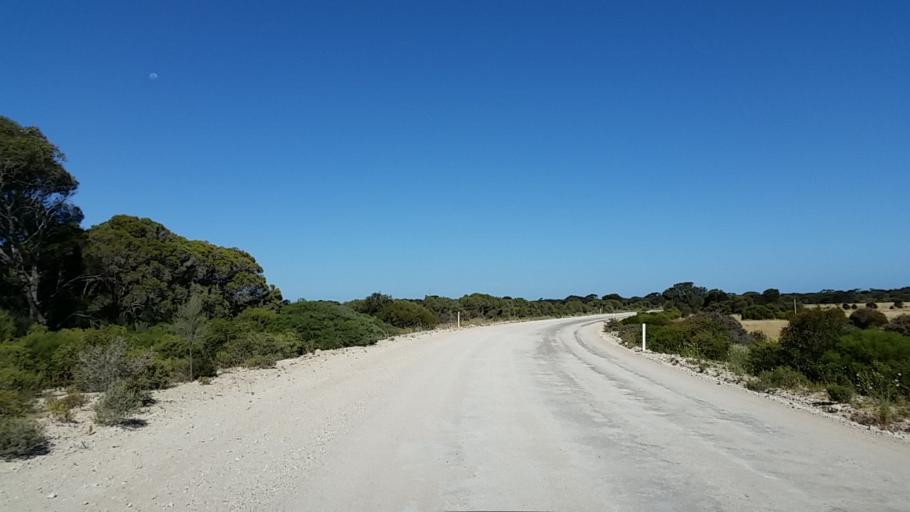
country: AU
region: South Australia
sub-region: Yorke Peninsula
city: Honiton
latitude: -35.2134
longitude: 137.0374
